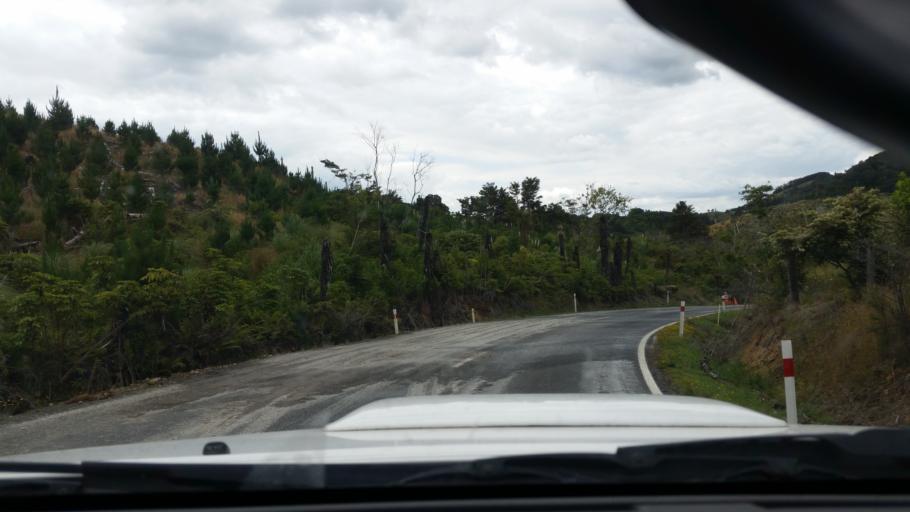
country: NZ
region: Northland
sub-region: Kaipara District
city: Dargaville
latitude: -35.7208
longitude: 173.8584
